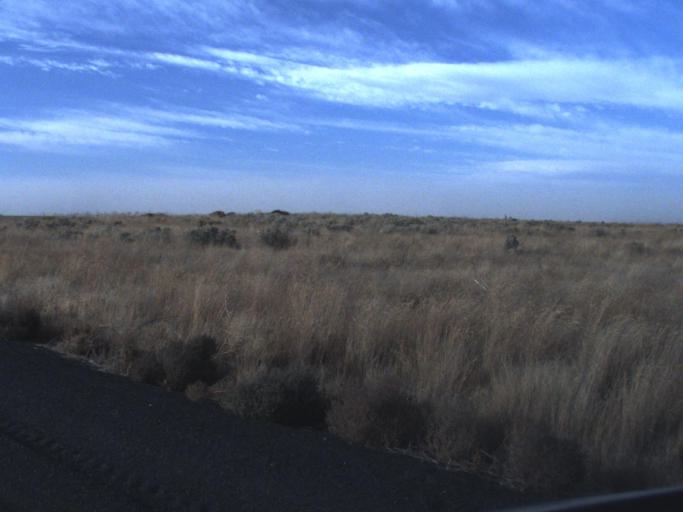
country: US
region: Washington
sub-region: Grant County
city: Warden
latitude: 47.3508
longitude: -118.9367
